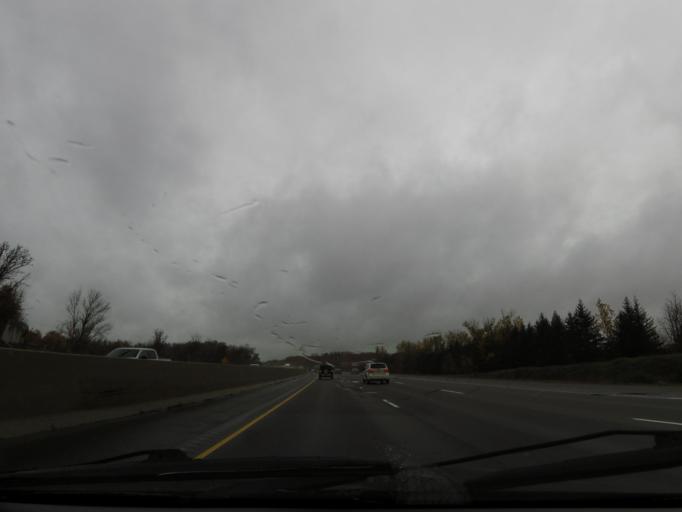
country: CA
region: Ontario
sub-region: Halton
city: Milton
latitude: 43.4727
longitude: -80.0411
